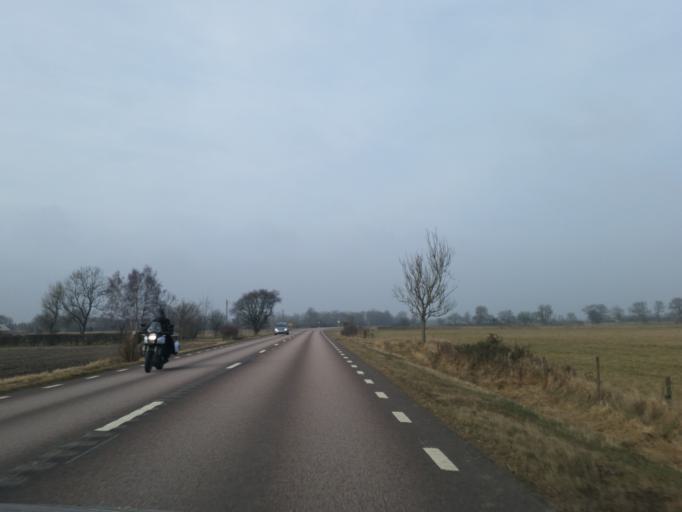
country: SE
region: Kalmar
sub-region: Borgholms Kommun
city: Borgholm
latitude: 57.1278
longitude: 16.9710
